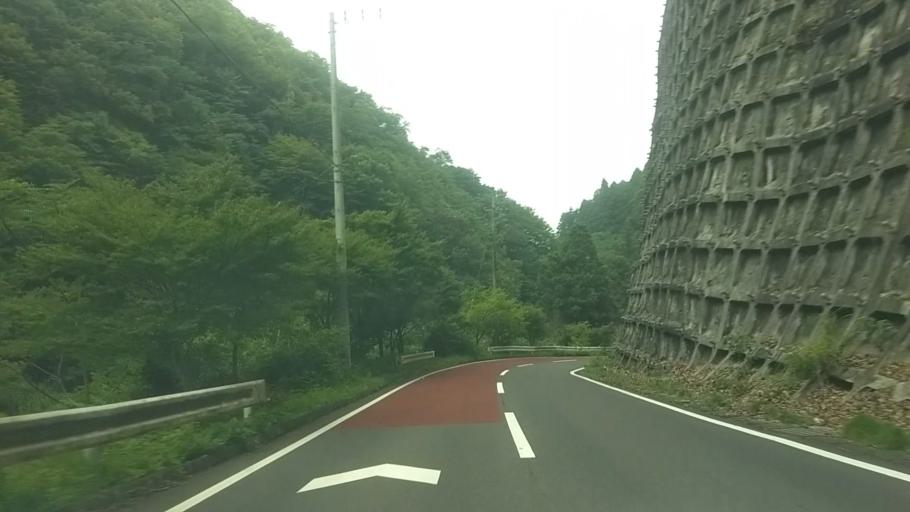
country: JP
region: Chiba
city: Kawaguchi
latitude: 35.2332
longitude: 140.0296
